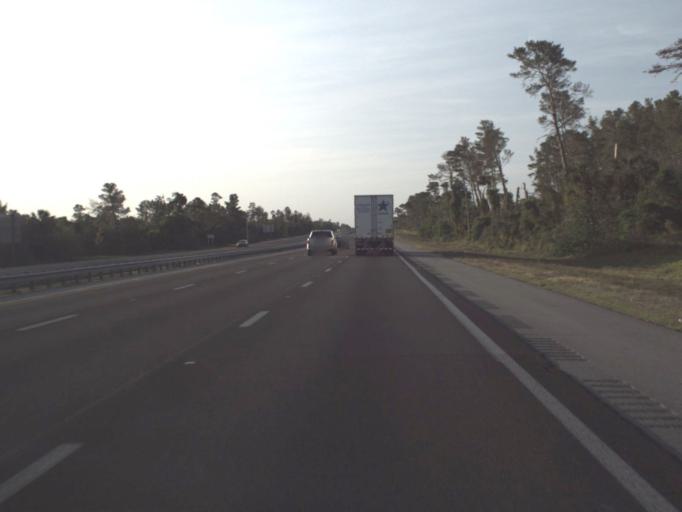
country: US
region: Florida
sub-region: Brevard County
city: Mims
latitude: 28.6273
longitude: -80.8536
